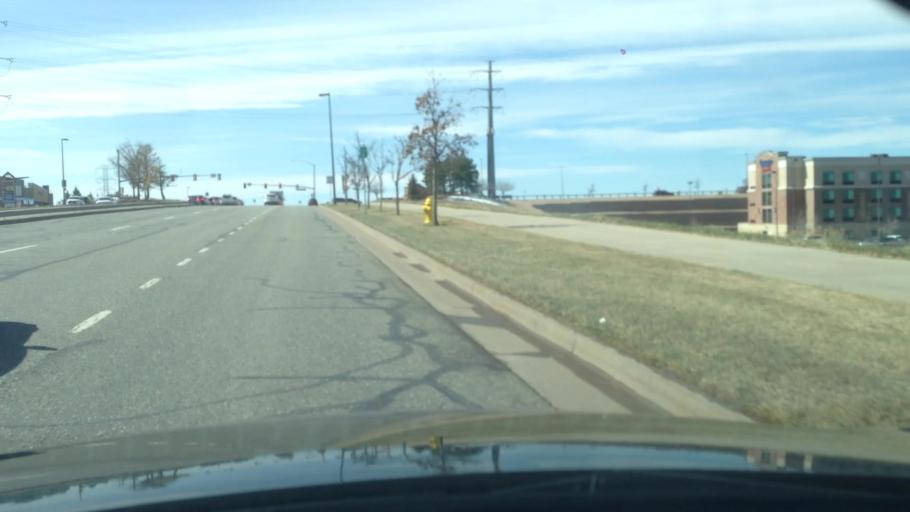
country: US
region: Colorado
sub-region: Douglas County
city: Parker
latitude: 39.5991
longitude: -104.7045
